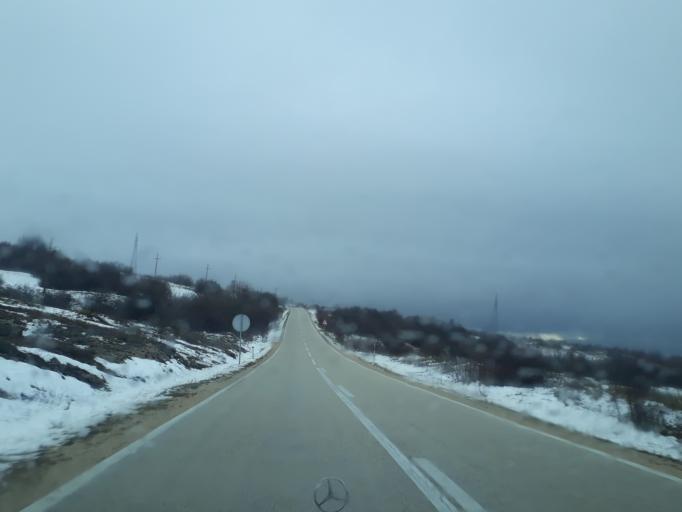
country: BA
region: Federation of Bosnia and Herzegovina
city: Tomislavgrad
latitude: 43.7908
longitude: 17.2200
